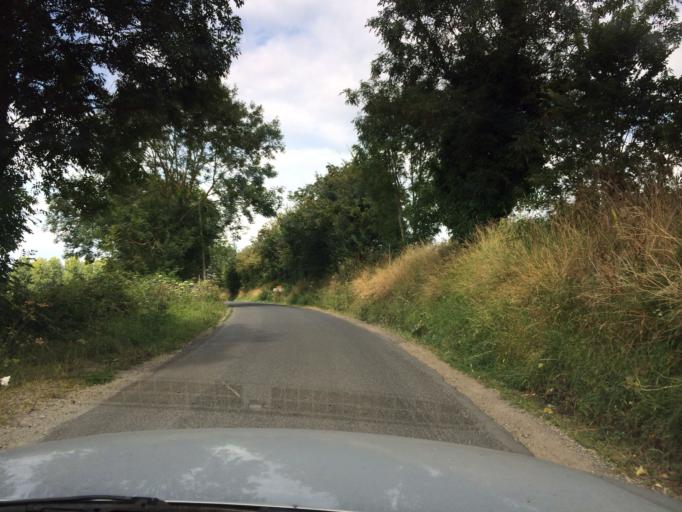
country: FR
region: Lower Normandy
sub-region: Departement du Calvados
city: Bayeux
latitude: 49.2865
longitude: -0.7354
